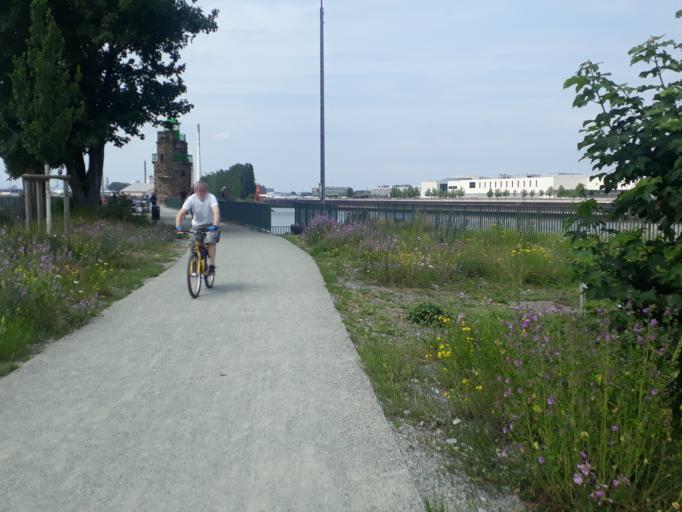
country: DE
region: Bremen
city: Bremen
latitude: 53.1054
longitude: 8.7486
